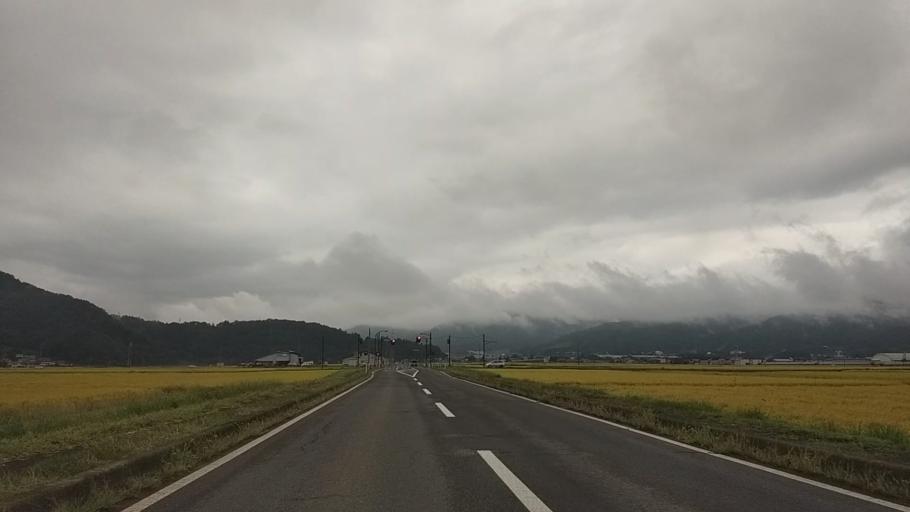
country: JP
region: Nagano
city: Iiyama
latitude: 36.8497
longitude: 138.3860
